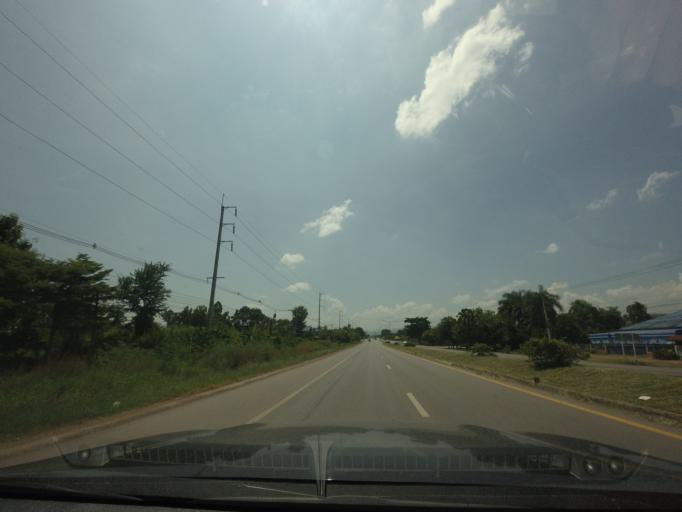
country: TH
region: Phetchabun
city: Lom Sak
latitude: 16.7232
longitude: 101.1850
